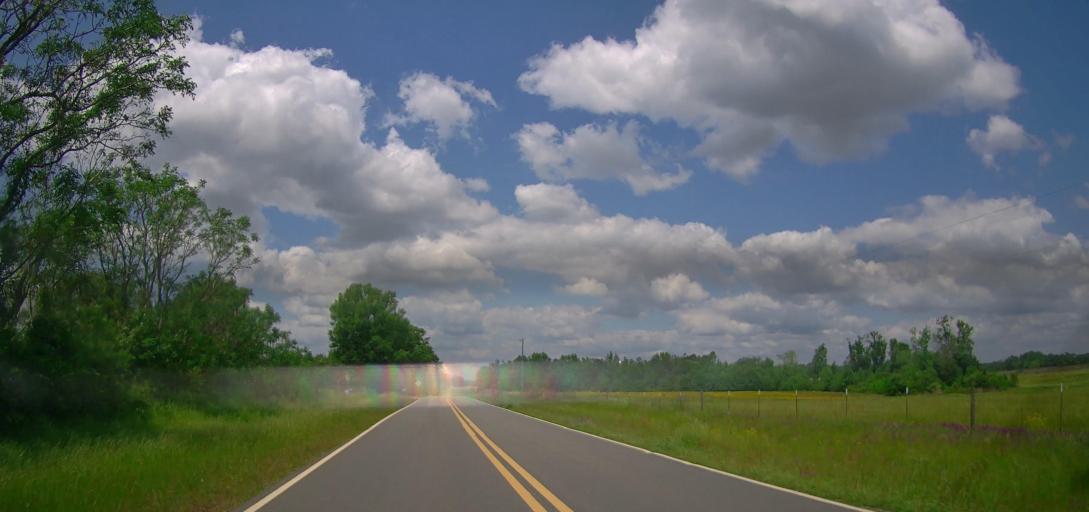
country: US
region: Georgia
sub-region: Laurens County
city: East Dublin
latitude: 32.6333
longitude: -82.8376
